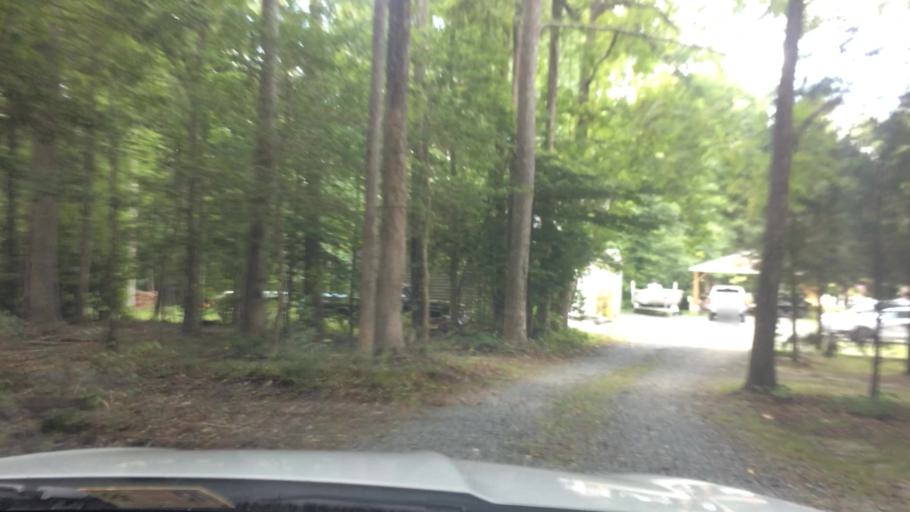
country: US
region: Virginia
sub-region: King William County
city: West Point
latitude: 37.5908
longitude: -76.7929
